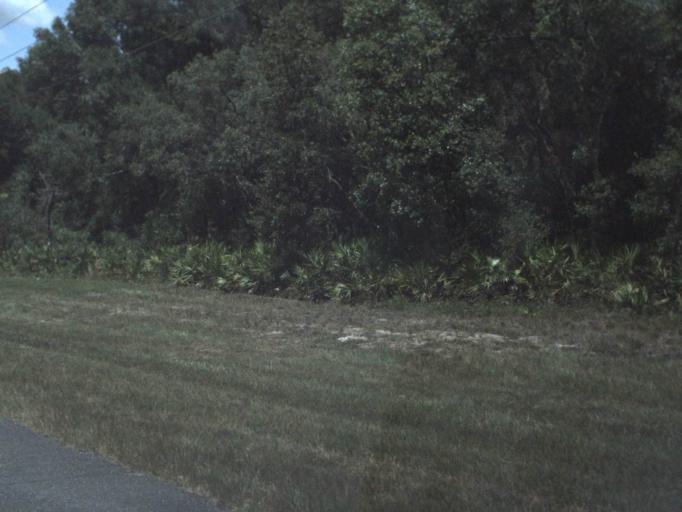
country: US
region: Florida
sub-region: Dixie County
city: Cross City
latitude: 29.6937
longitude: -82.9843
